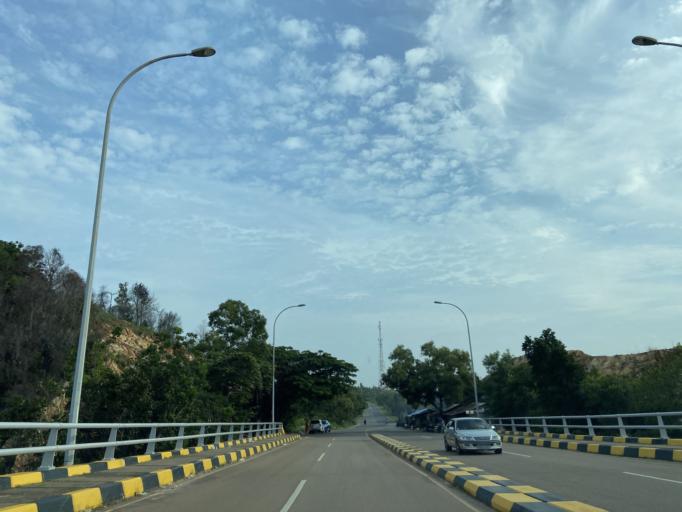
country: ID
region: Riau Islands
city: Tanjungpinang
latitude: 0.9473
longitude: 104.0778
